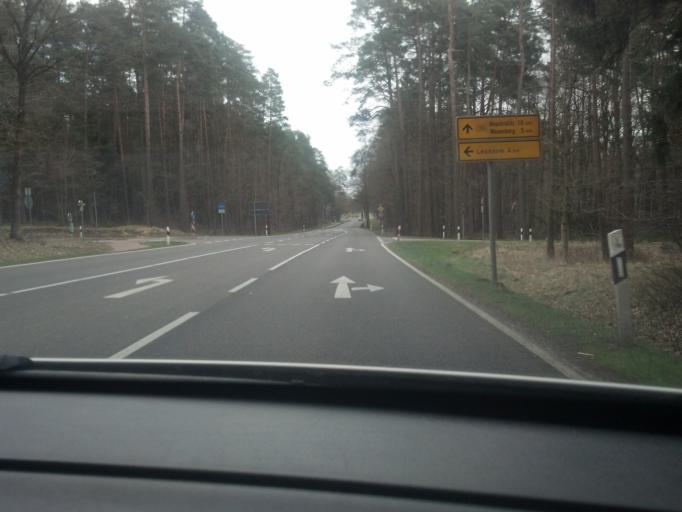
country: DE
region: Mecklenburg-Vorpommern
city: Wesenberg
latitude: 53.2705
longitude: 12.8851
